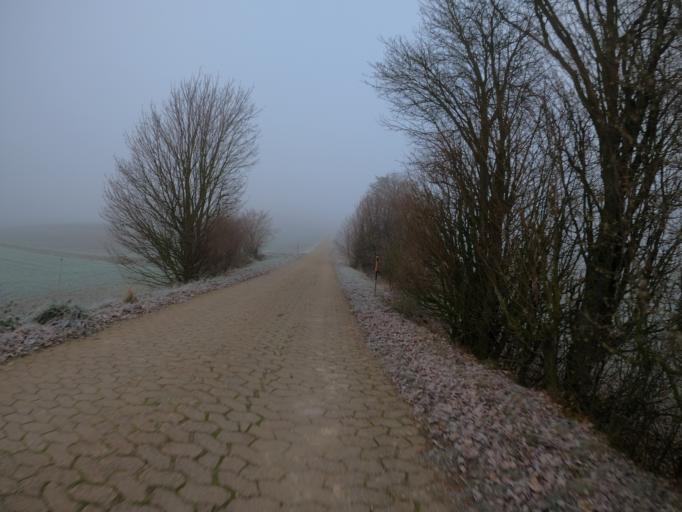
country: DE
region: Baden-Wuerttemberg
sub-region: Tuebingen Region
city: Beimerstetten
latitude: 48.4853
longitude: 9.9737
